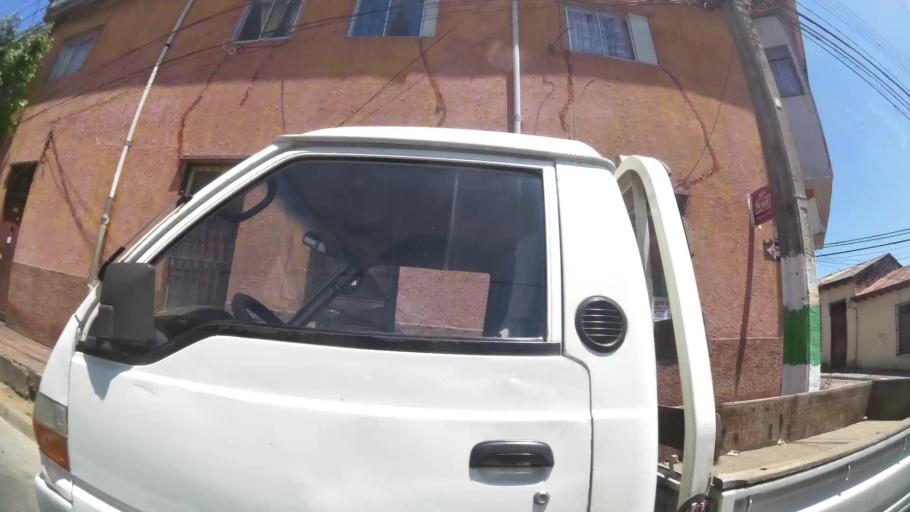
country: CL
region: Valparaiso
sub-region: Provincia de Valparaiso
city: Valparaiso
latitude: -33.0363
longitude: -71.6393
